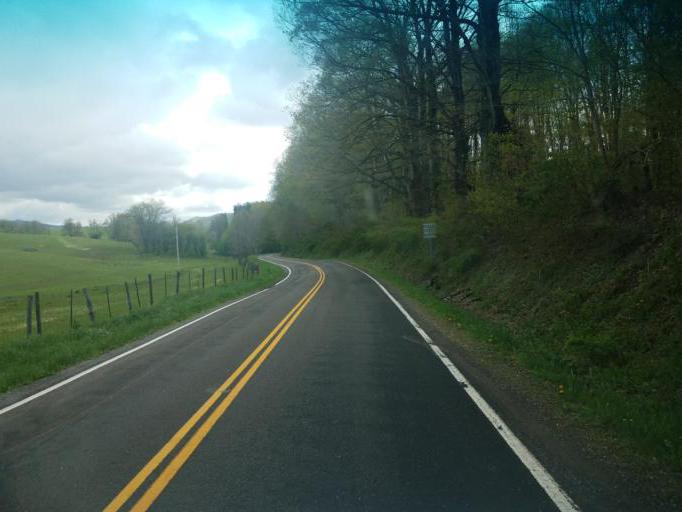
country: US
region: Virginia
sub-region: Wythe County
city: Rural Retreat
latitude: 37.0153
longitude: -81.3536
